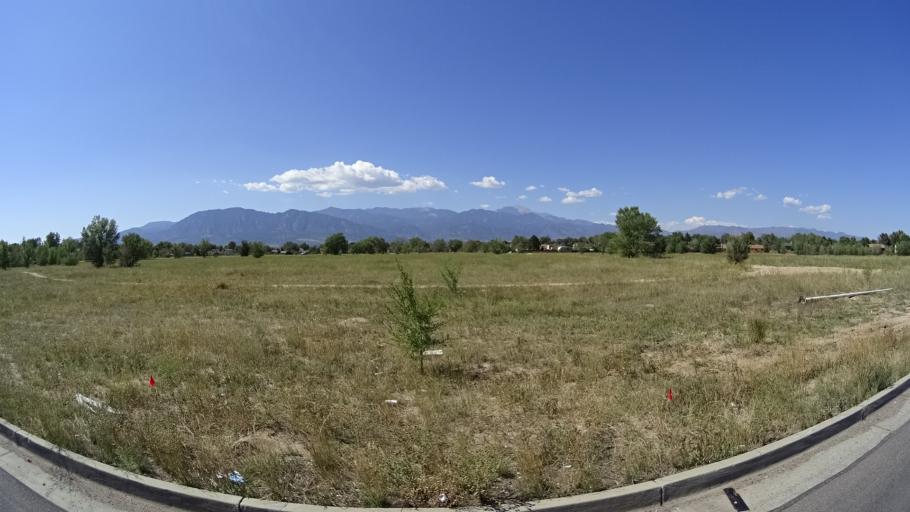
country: US
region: Colorado
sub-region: El Paso County
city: Stratmoor
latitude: 38.7887
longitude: -104.7390
